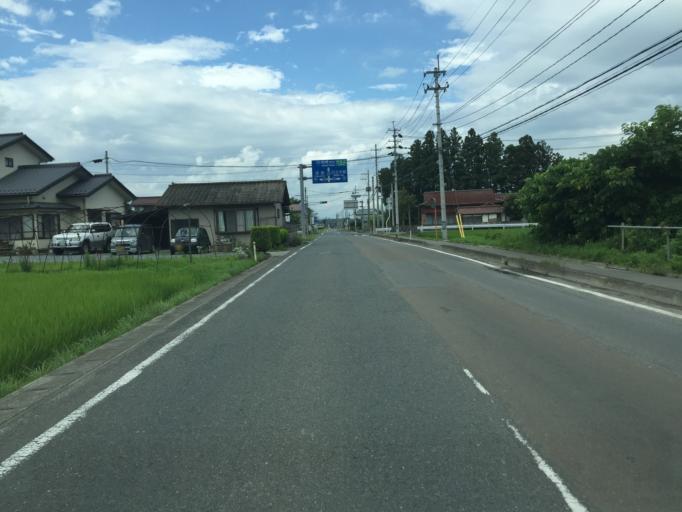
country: JP
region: Miyagi
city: Marumori
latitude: 37.7692
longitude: 140.9142
